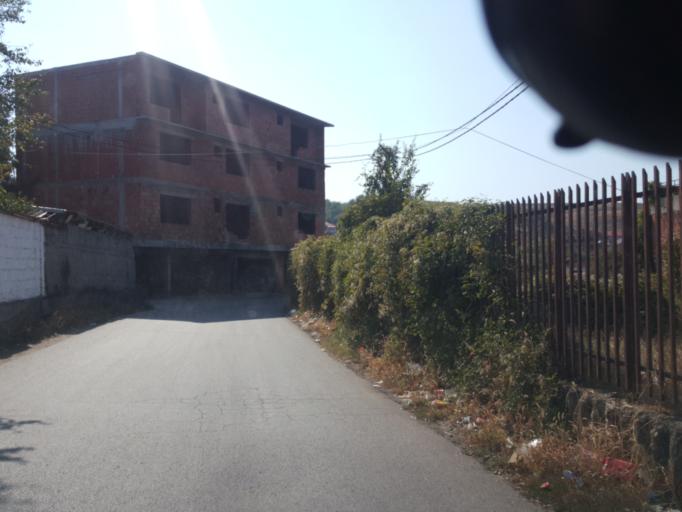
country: XK
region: Gjakova
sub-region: Komuna e Gjakoves
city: Gjakove
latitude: 42.3916
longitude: 20.4231
